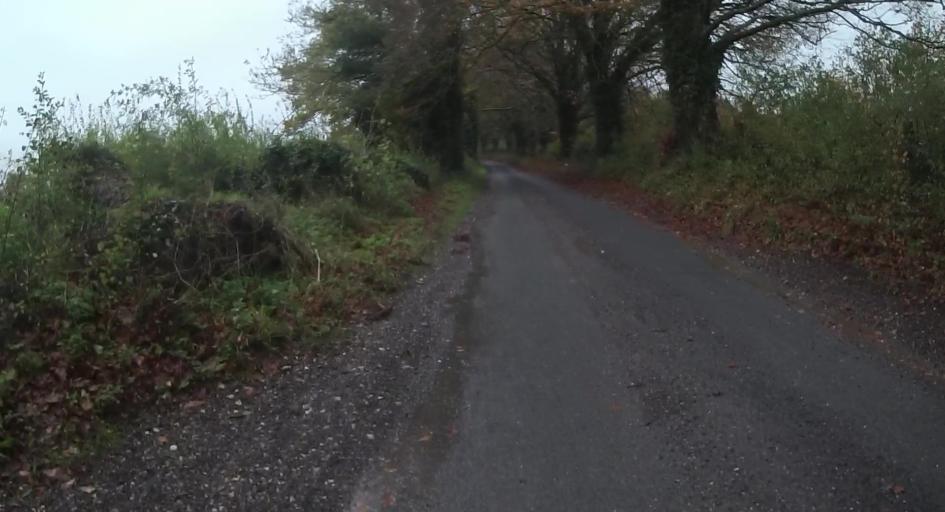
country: GB
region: England
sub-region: Hampshire
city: Four Marks
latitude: 51.1508
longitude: -1.1167
